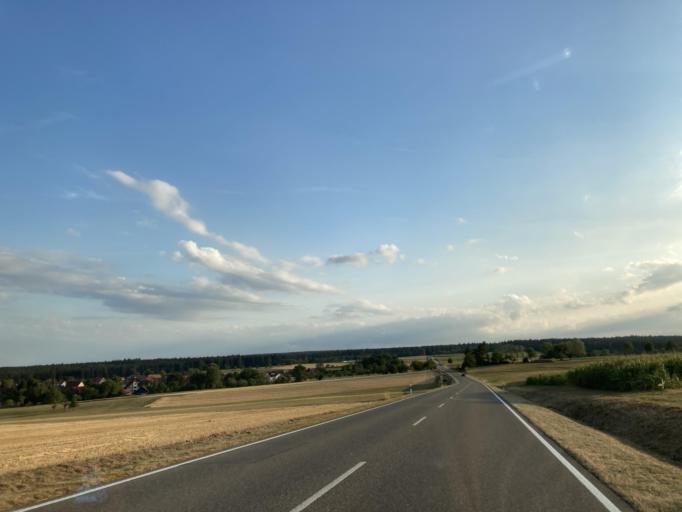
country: DE
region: Baden-Wuerttemberg
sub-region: Karlsruhe Region
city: Pfalzgrafenweiler
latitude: 48.5269
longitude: 8.5508
